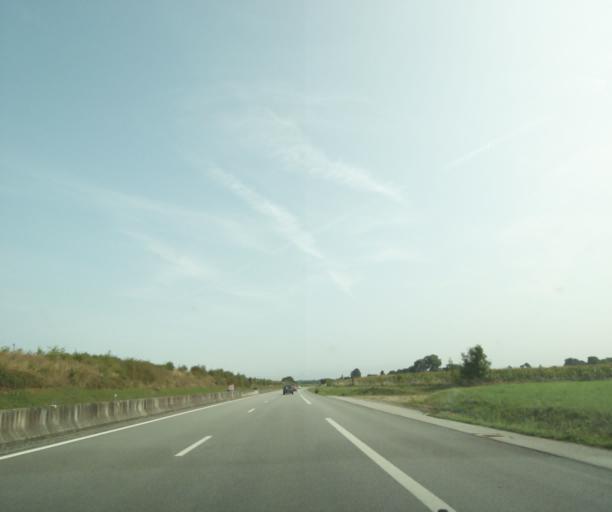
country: FR
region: Lower Normandy
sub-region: Departement de l'Orne
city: Radon
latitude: 48.5095
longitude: 0.1328
